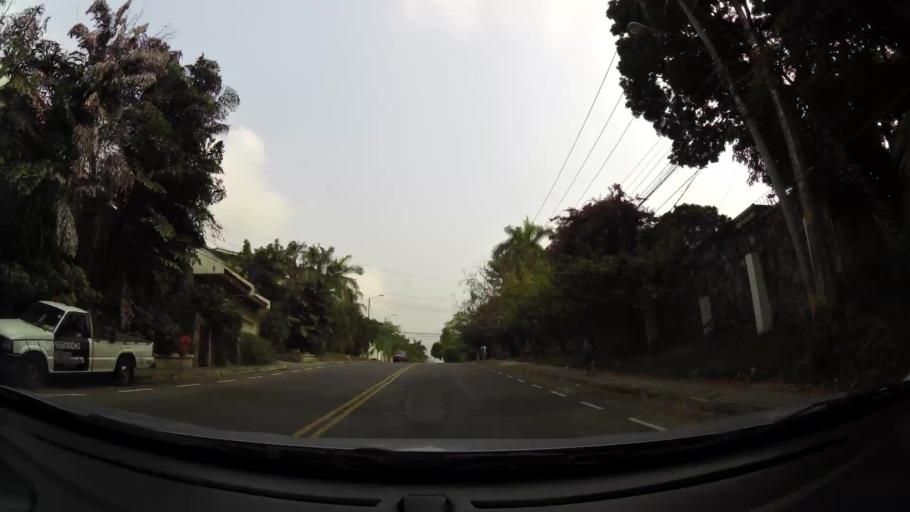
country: HN
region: Cortes
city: El Zapotal del Norte
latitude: 15.5086
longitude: -88.0480
